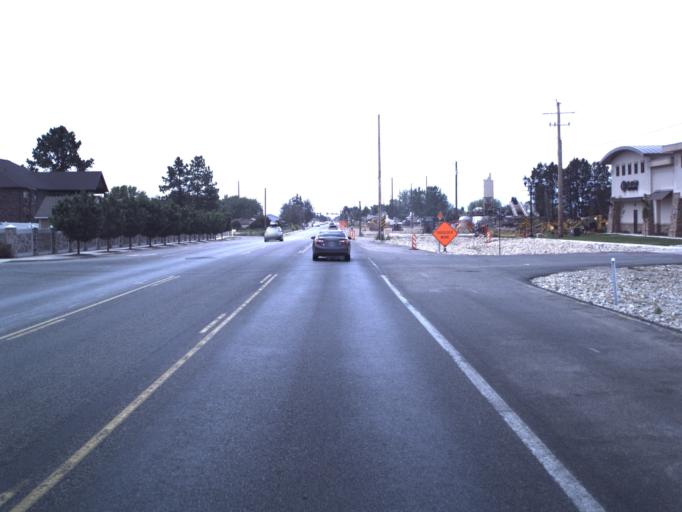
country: US
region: Utah
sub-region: Davis County
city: West Point
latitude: 41.1154
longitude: -112.0646
